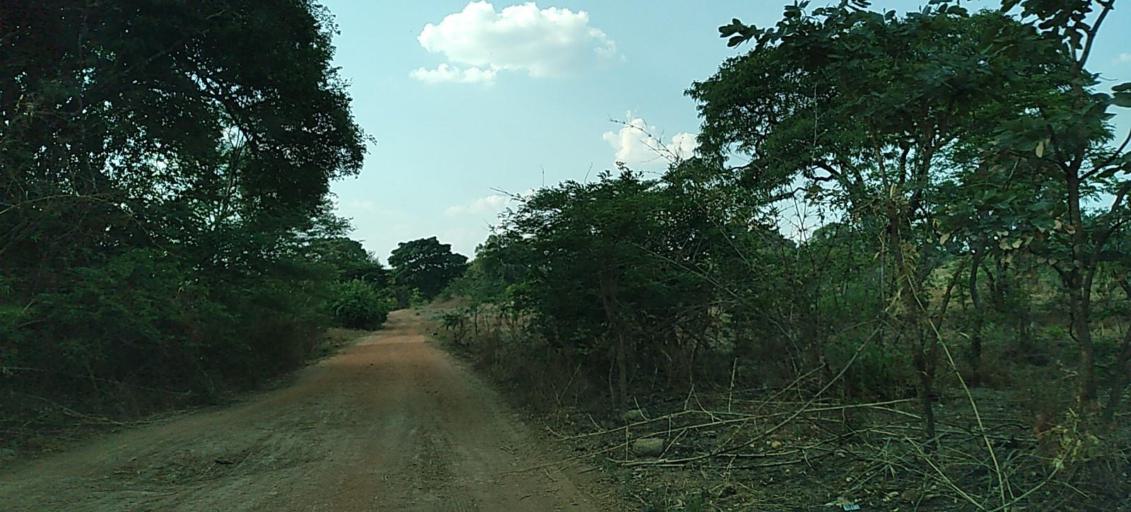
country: ZM
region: Copperbelt
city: Mpongwe
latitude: -13.4798
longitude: 28.0838
